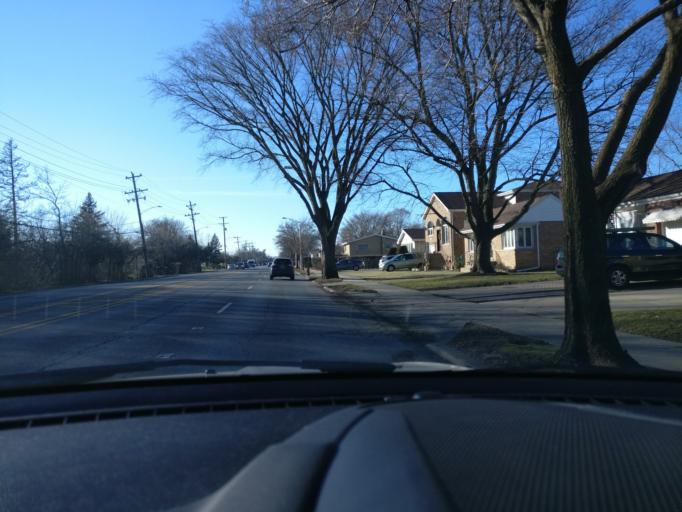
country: US
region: Illinois
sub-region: Cook County
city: Skokie
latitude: 42.0408
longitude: -87.7356
